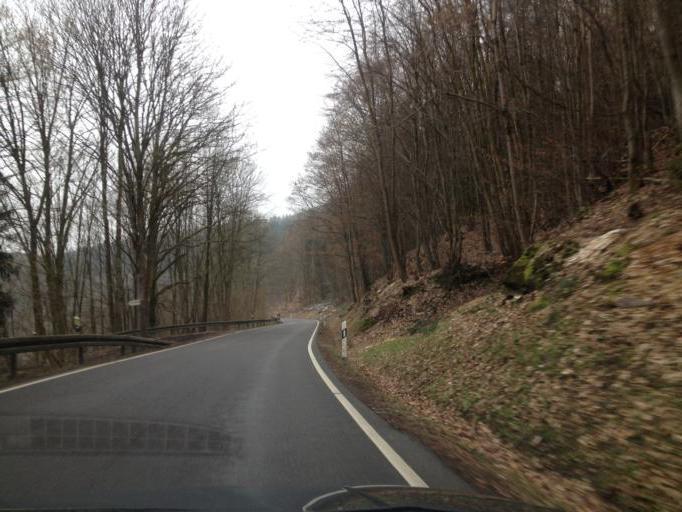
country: DE
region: Saarland
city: Hangard
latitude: 49.4009
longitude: 7.2160
